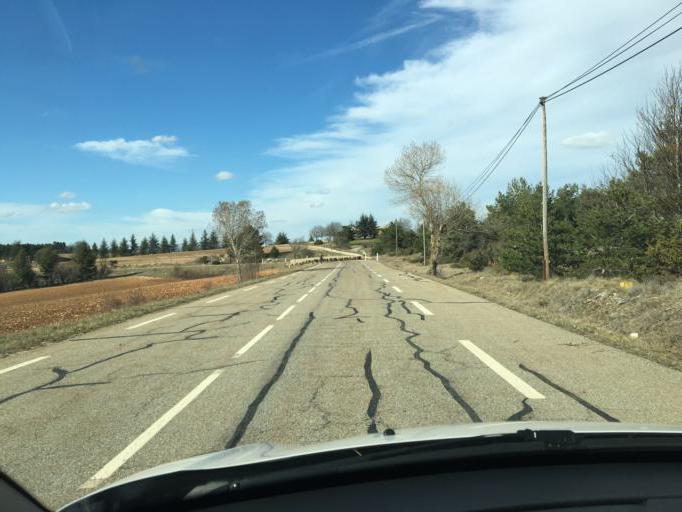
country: FR
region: Provence-Alpes-Cote d'Azur
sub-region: Departement du Vaucluse
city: Sault
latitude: 44.0021
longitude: 5.4838
